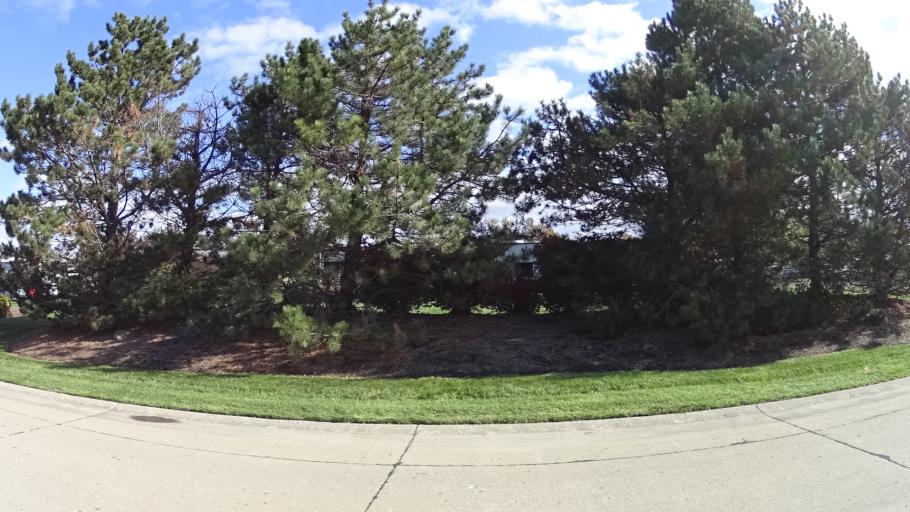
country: US
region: Ohio
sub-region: Lorain County
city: Lorain
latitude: 41.4464
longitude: -82.2125
